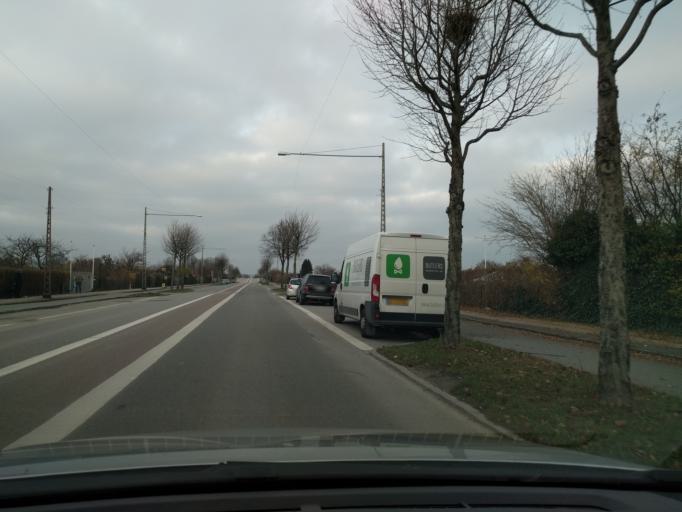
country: DK
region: Capital Region
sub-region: Tarnby Kommune
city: Tarnby
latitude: 55.6245
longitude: 12.5868
